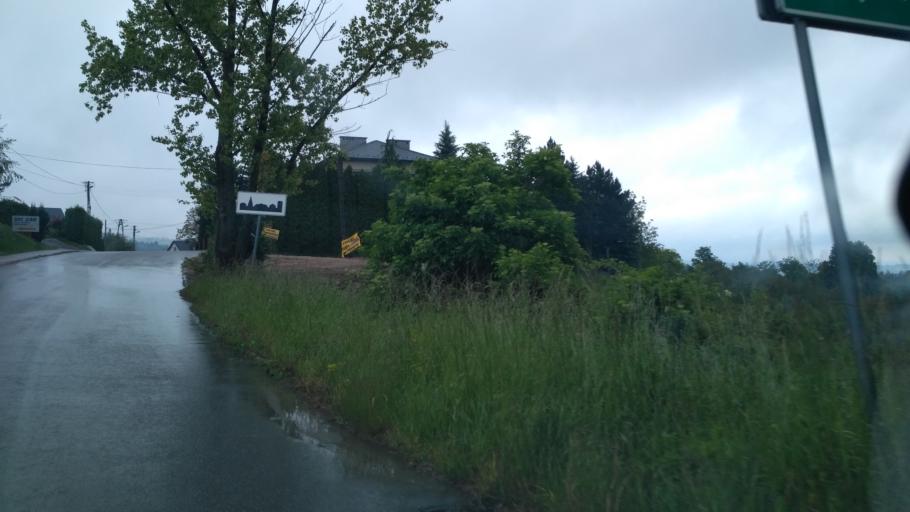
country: PL
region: Subcarpathian Voivodeship
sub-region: Powiat jasielski
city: Jaslo
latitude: 49.7622
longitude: 21.4841
